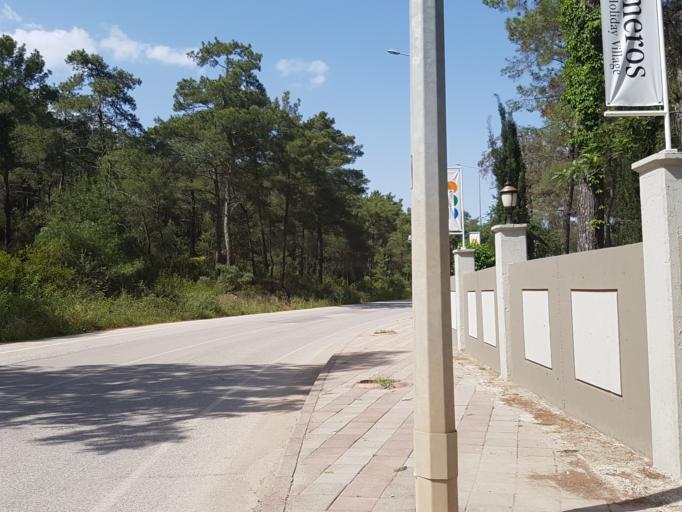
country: TR
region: Antalya
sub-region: Kemer
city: Goeynuek
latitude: 36.6486
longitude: 30.5509
